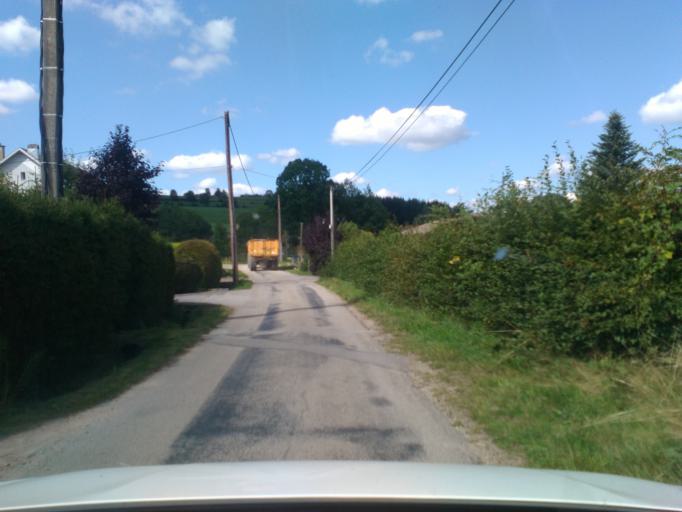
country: FR
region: Lorraine
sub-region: Departement des Vosges
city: Corcieux
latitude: 48.1479
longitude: 6.9179
